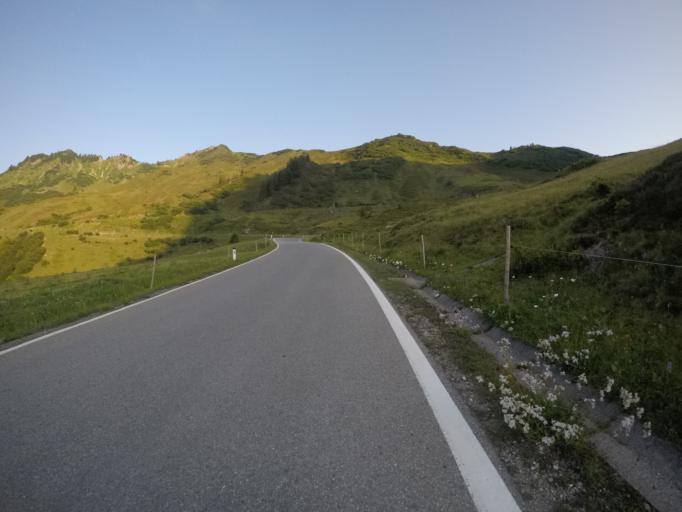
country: AT
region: Vorarlberg
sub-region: Politischer Bezirk Bregenz
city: Damuels
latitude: 47.2773
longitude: 9.8401
